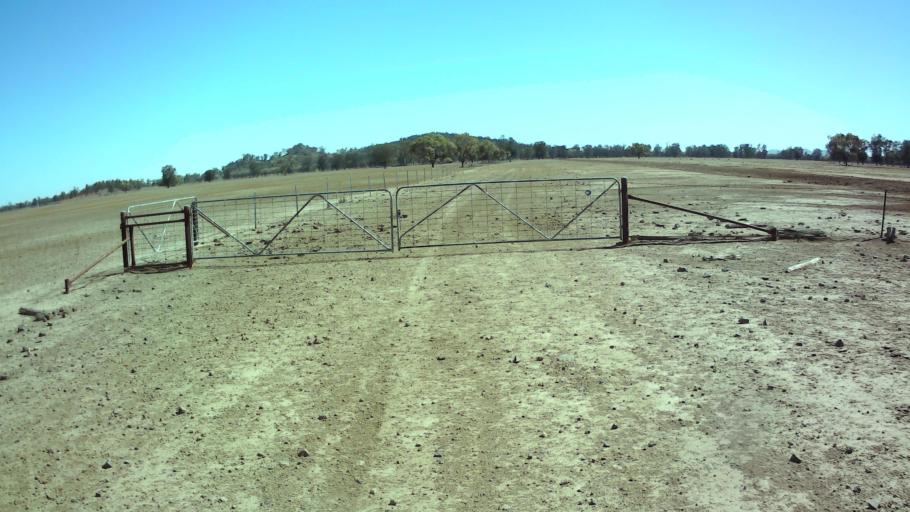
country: AU
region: New South Wales
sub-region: Bland
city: West Wyalong
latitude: -33.7501
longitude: 147.6600
